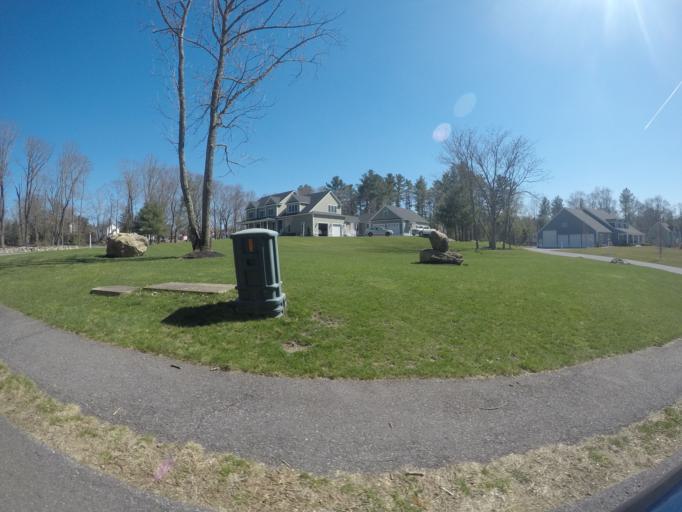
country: US
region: Massachusetts
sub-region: Norfolk County
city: Stoughton
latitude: 42.0790
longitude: -71.0905
